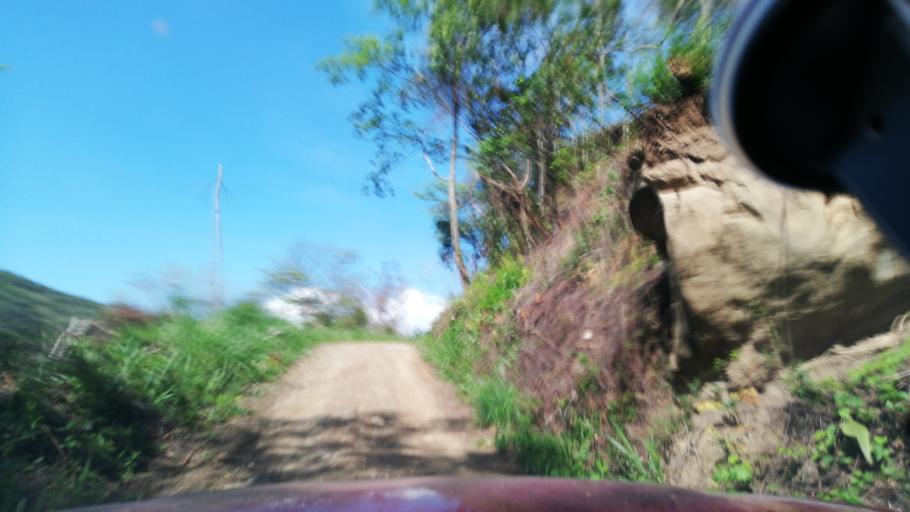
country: CO
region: Cundinamarca
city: Quipile
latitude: 4.7571
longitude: -74.6171
